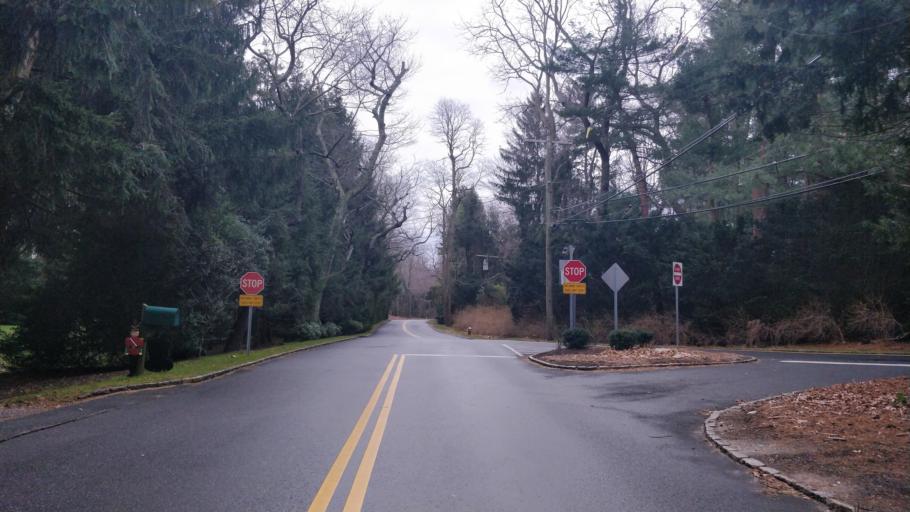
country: US
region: New York
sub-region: Nassau County
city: Laurel Hollow
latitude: 40.8534
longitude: -73.4747
